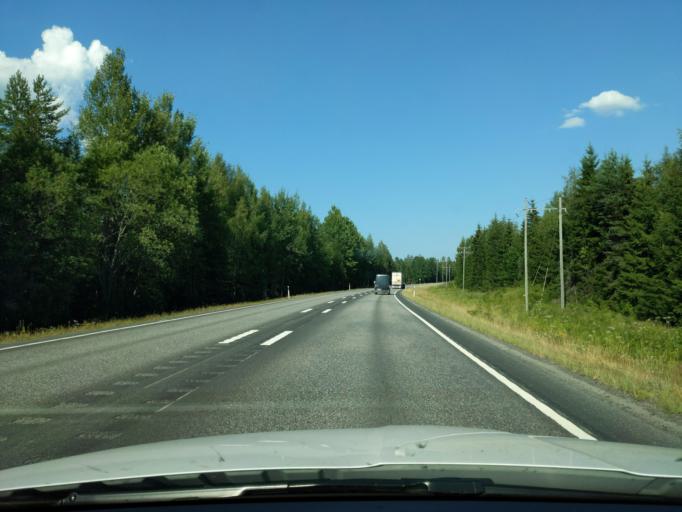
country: FI
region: Paijanne Tavastia
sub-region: Lahti
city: Hollola
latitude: 60.9357
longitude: 25.3888
